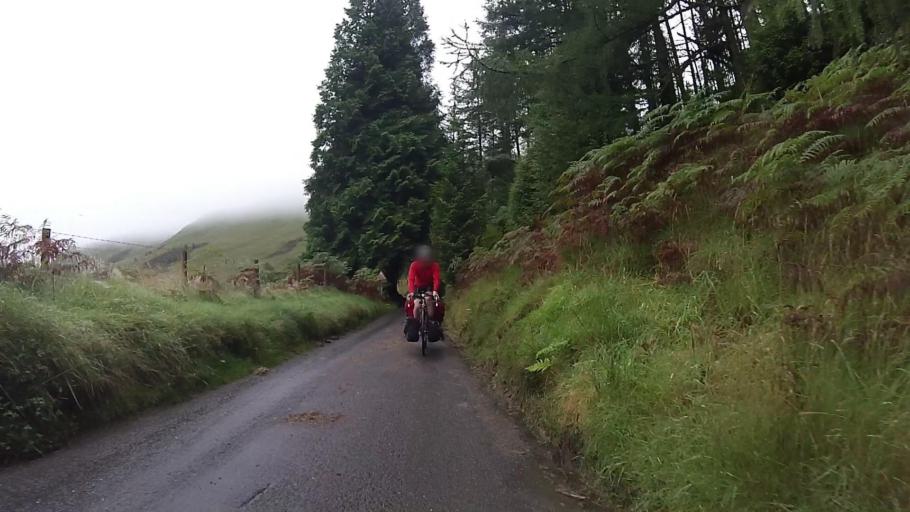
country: GB
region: Wales
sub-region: Carmarthenshire
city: Llandovery
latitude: 52.1878
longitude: -3.7108
